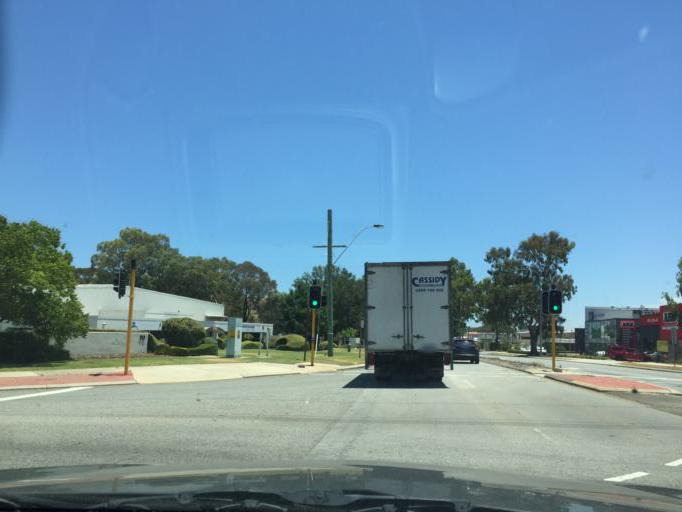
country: AU
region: Western Australia
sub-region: Canning
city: Canning Vale
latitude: -32.0611
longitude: 115.9223
